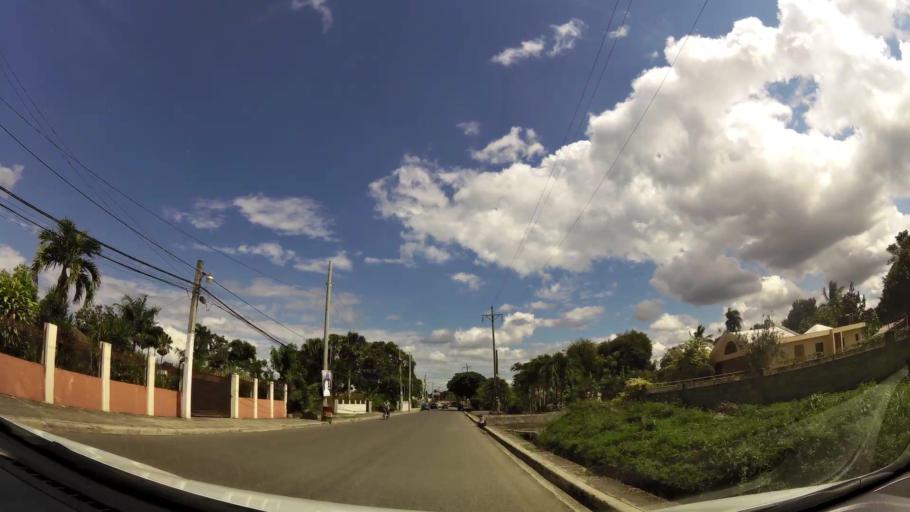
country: DO
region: Santiago
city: Licey al Medio
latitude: 19.3807
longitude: -70.6167
